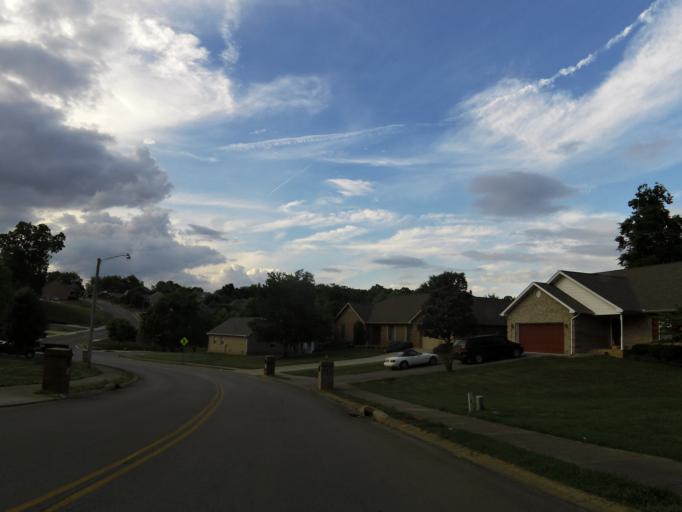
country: US
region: Tennessee
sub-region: Blount County
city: Maryville
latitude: 35.7566
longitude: -83.9465
